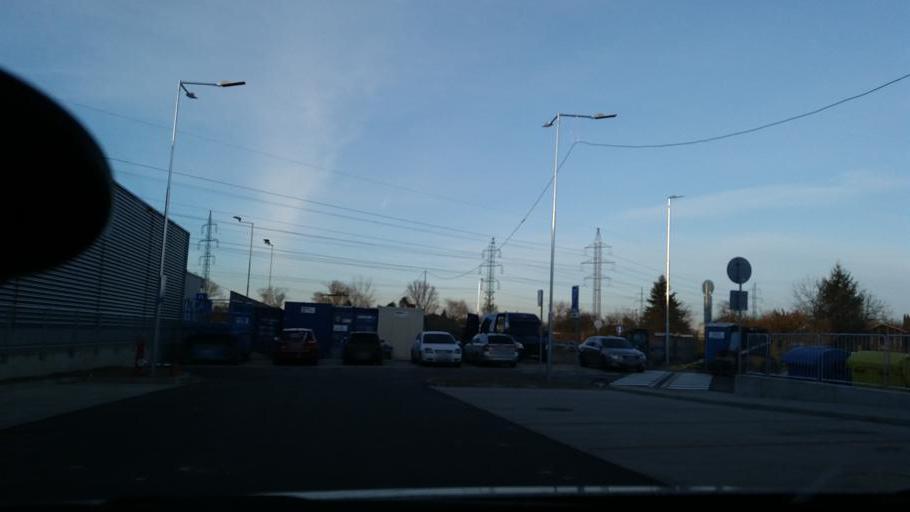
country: SK
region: Bratislavsky
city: Dunajska Luzna
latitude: 48.1316
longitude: 17.1916
